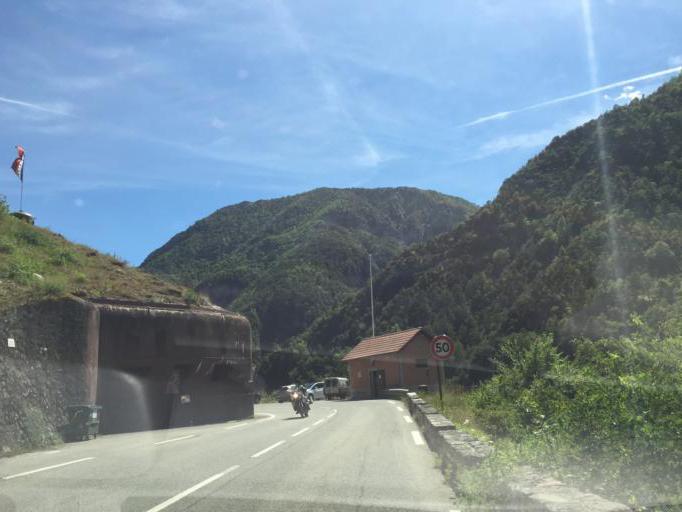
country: FR
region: Provence-Alpes-Cote d'Azur
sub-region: Departement des Alpes-Maritimes
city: Saint-Martin-Vesubie
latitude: 44.0631
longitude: 7.1171
